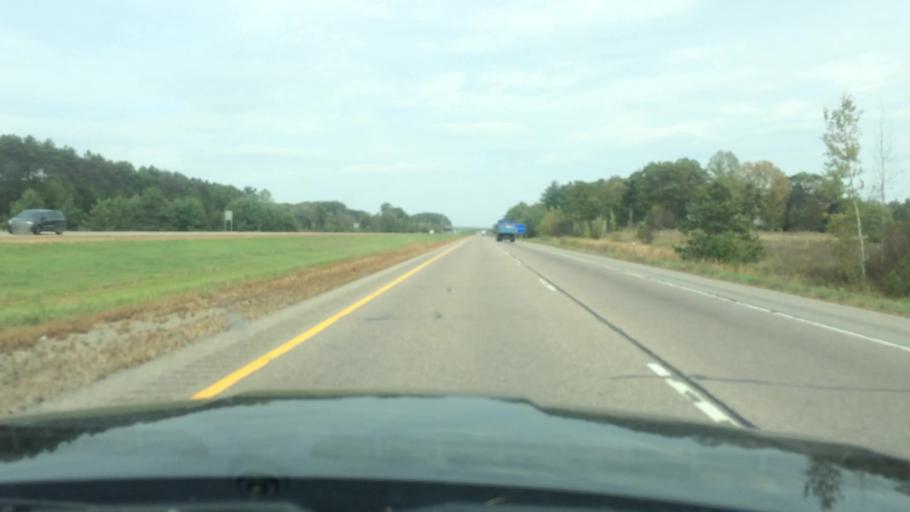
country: US
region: Wisconsin
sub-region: Marathon County
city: Mosinee
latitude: 44.6650
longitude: -89.6426
